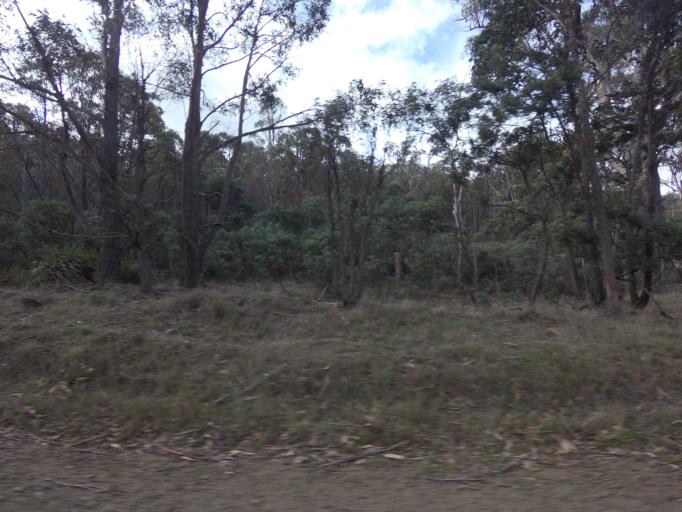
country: AU
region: Tasmania
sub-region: Brighton
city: Bridgewater
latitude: -42.4843
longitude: 147.3020
